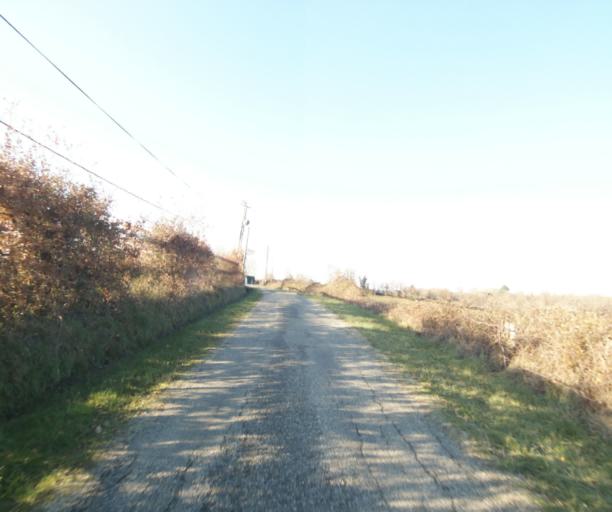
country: FR
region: Midi-Pyrenees
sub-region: Departement du Tarn-et-Garonne
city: Moissac
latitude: 44.1440
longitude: 1.0668
